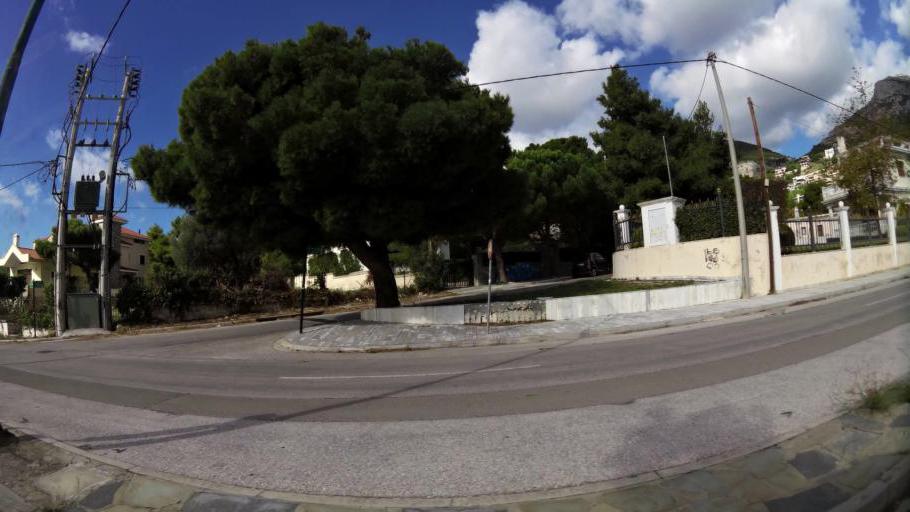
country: GR
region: Attica
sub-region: Nomarchia Anatolikis Attikis
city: Thrakomakedones
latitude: 38.1383
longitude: 23.7516
